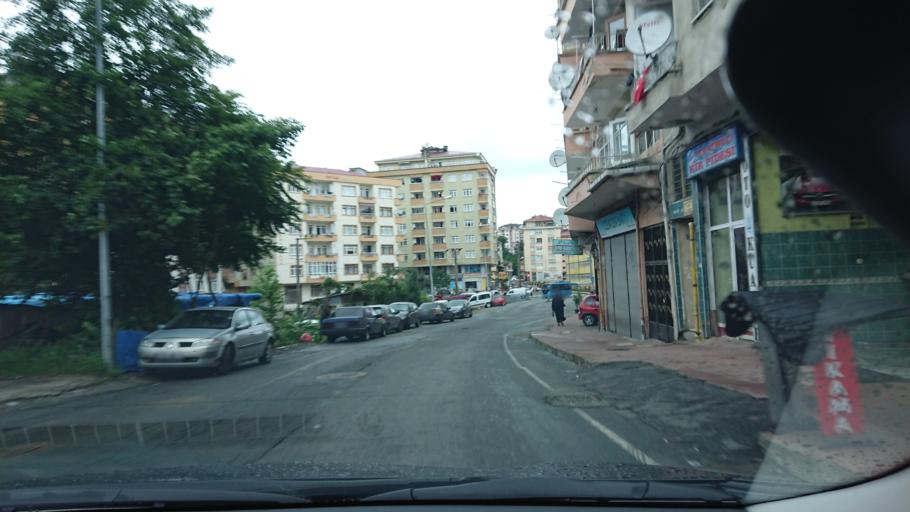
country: TR
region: Rize
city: Rize
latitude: 41.0303
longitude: 40.5109
